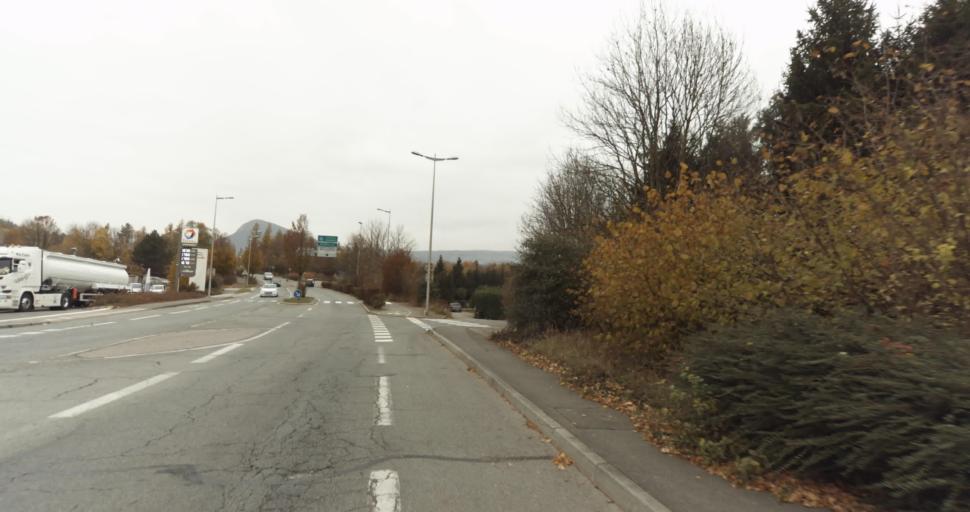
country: FR
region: Rhone-Alpes
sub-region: Departement de la Haute-Savoie
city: Meythet
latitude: 45.9243
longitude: 6.0890
